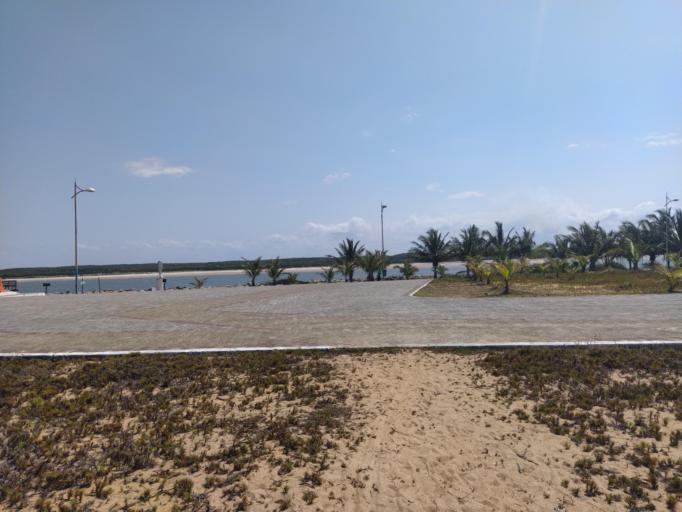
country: BR
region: Espirito Santo
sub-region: Conceicao Da Barra
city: Conceicao da Barra
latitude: -18.5998
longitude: -39.7278
